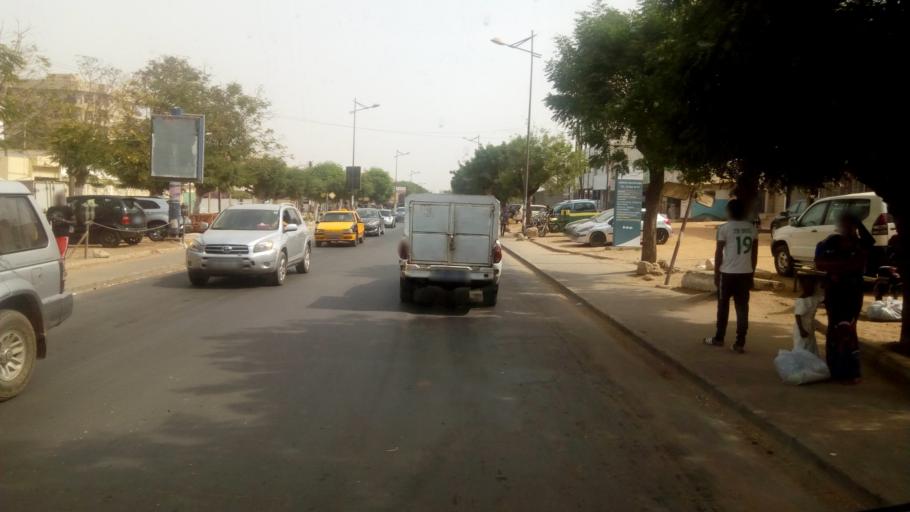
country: SN
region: Dakar
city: Grand Dakar
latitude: 14.7182
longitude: -17.4503
